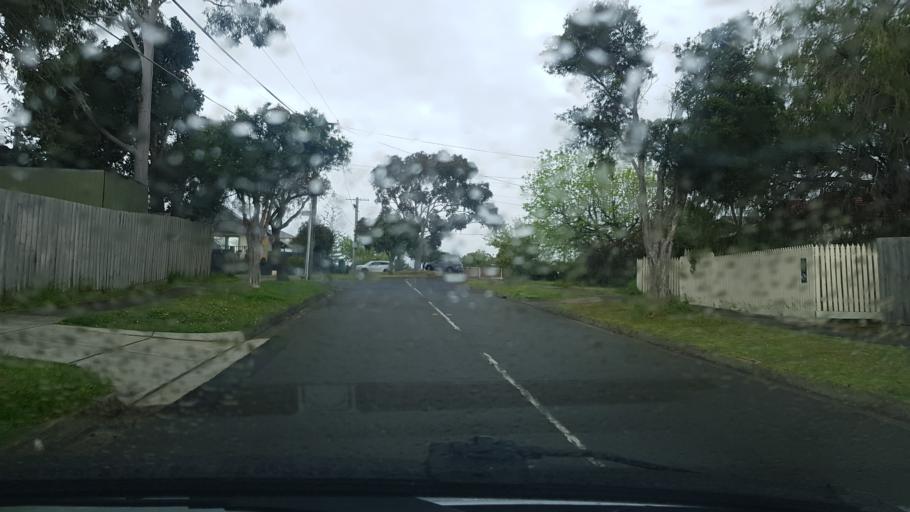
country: AU
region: Victoria
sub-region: Greater Dandenong
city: Springvale
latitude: -37.9274
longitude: 145.1510
